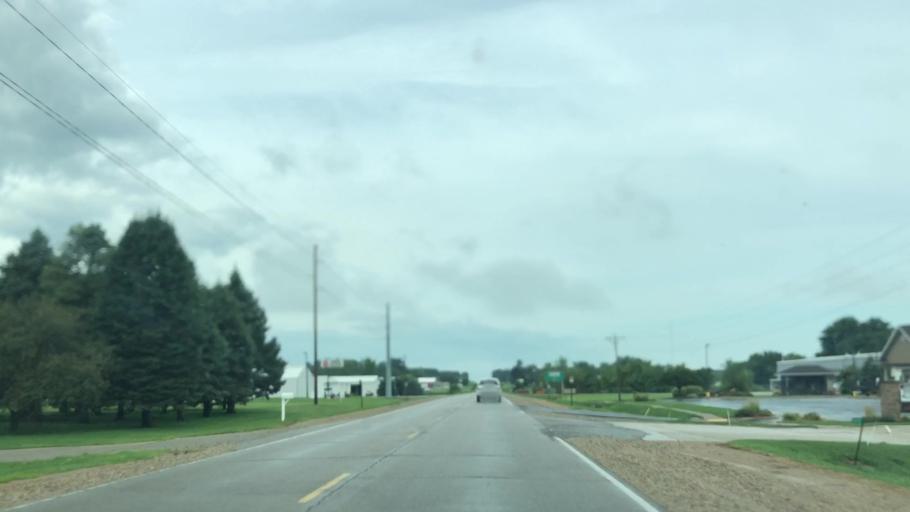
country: US
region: Iowa
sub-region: Marshall County
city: Marshalltown
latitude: 42.0073
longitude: -92.9324
